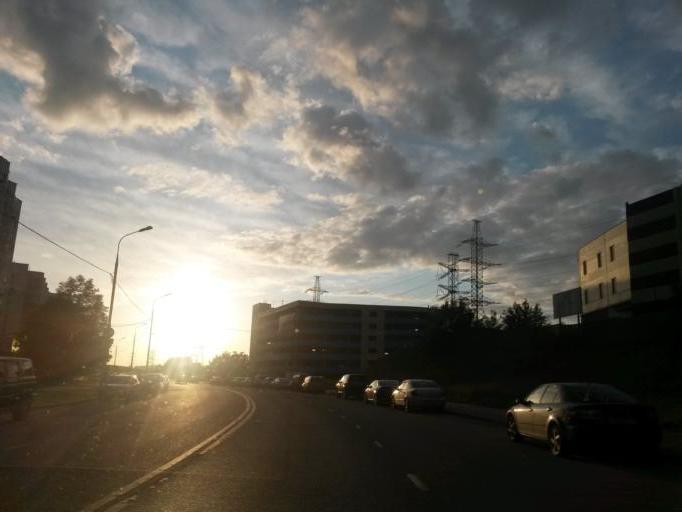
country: RU
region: Moscow
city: Annino
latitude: 55.5747
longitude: 37.5908
